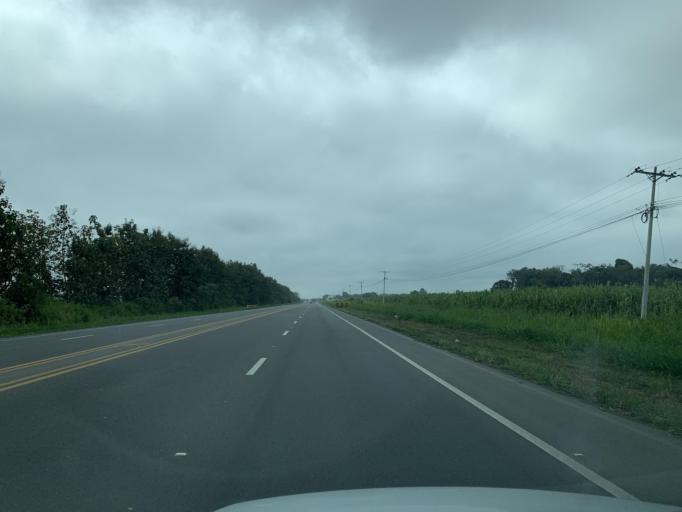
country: EC
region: Guayas
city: Coronel Marcelino Mariduena
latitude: -2.3103
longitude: -79.4772
